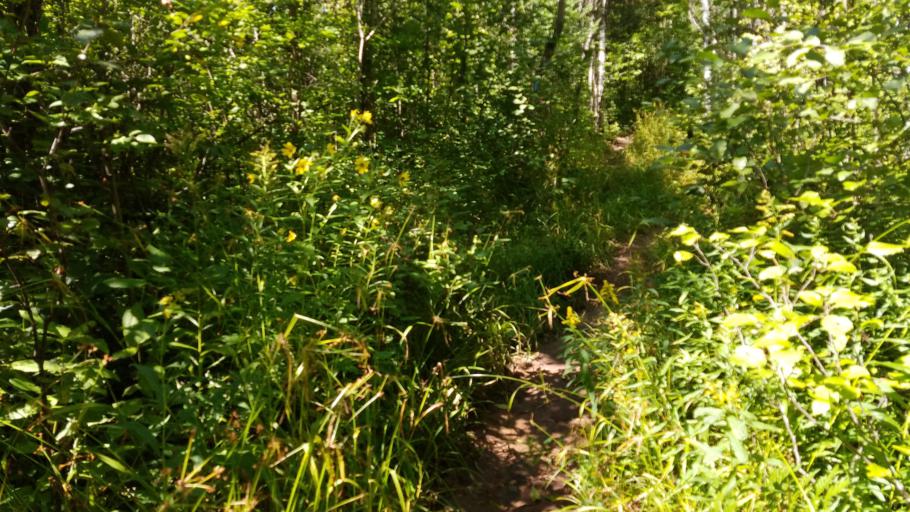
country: US
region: Michigan
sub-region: Ontonagon County
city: Ontonagon
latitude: 46.6507
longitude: -89.1567
